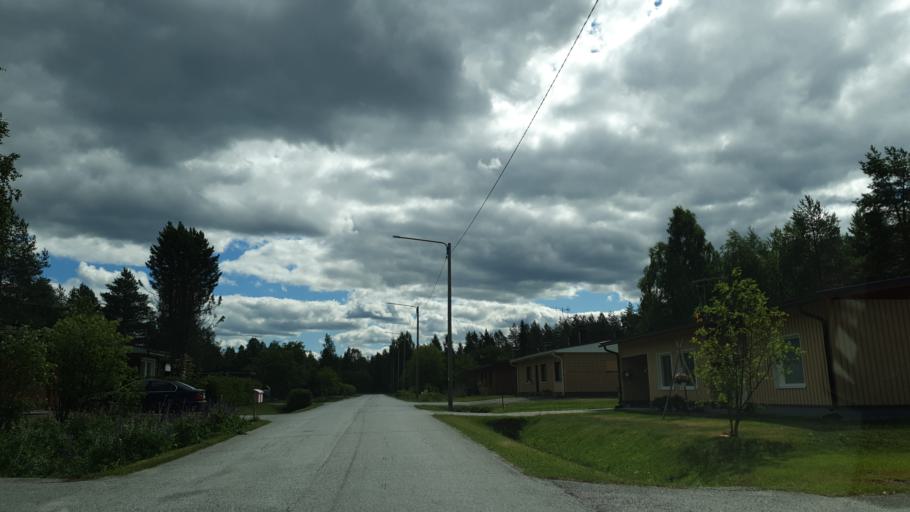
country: FI
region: Kainuu
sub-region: Kehys-Kainuu
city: Kuhmo
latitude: 64.1131
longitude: 29.4846
